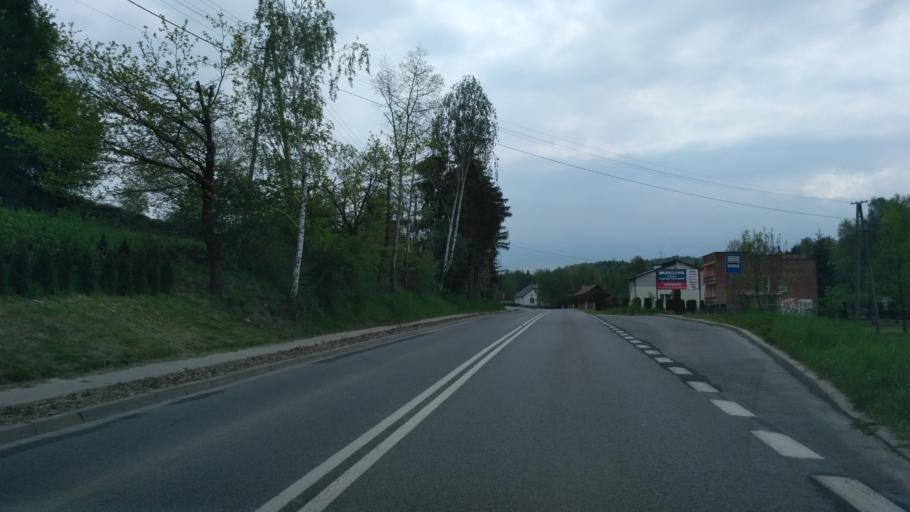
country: PL
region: Lesser Poland Voivodeship
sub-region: Powiat tarnowski
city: Tarnowiec
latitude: 49.9567
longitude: 21.0001
